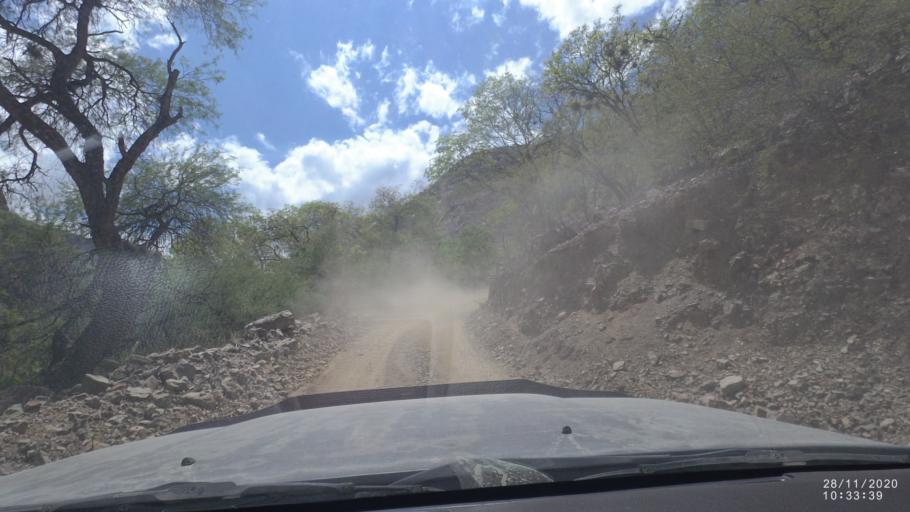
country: BO
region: Cochabamba
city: Capinota
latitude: -17.7963
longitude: -66.1352
